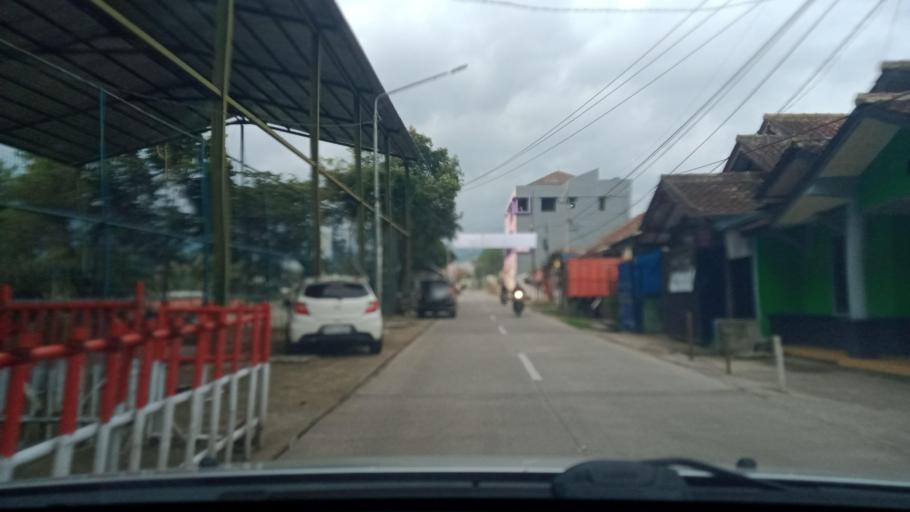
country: ID
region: West Java
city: Lembang
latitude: -6.8152
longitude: 107.5759
